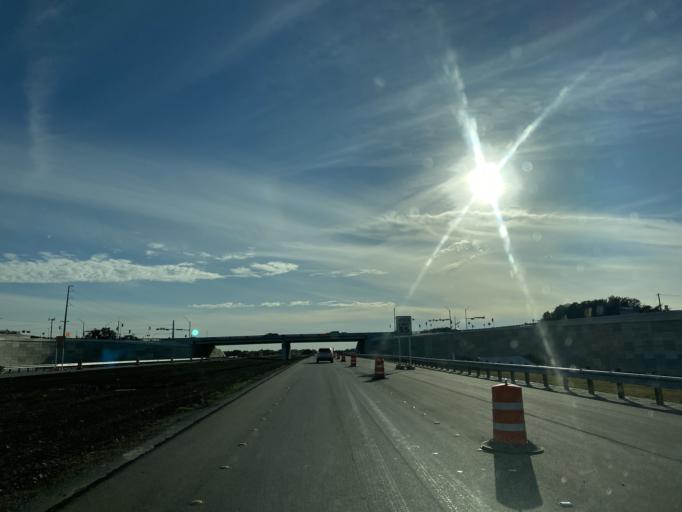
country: US
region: Texas
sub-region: Travis County
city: Shady Hollow
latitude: 30.2026
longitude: -97.8652
